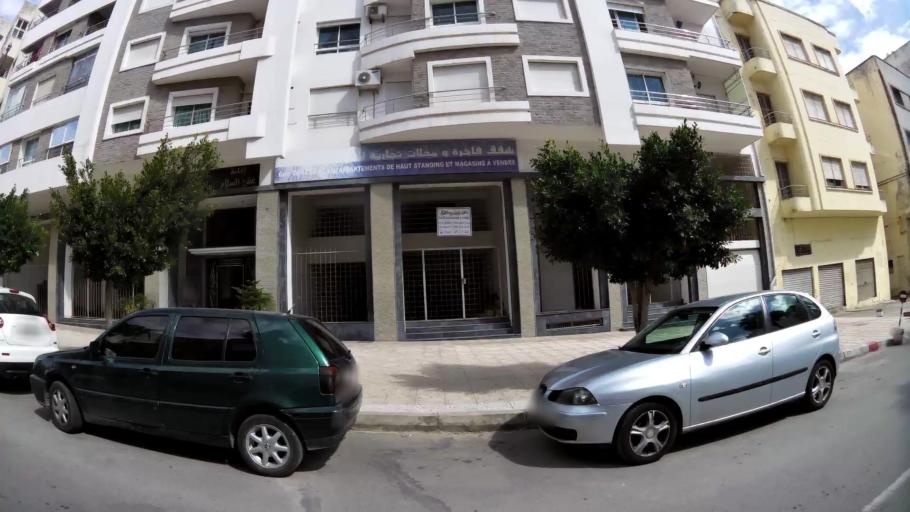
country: MA
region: Tanger-Tetouan
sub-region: Tanger-Assilah
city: Tangier
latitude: 35.7716
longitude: -5.8081
